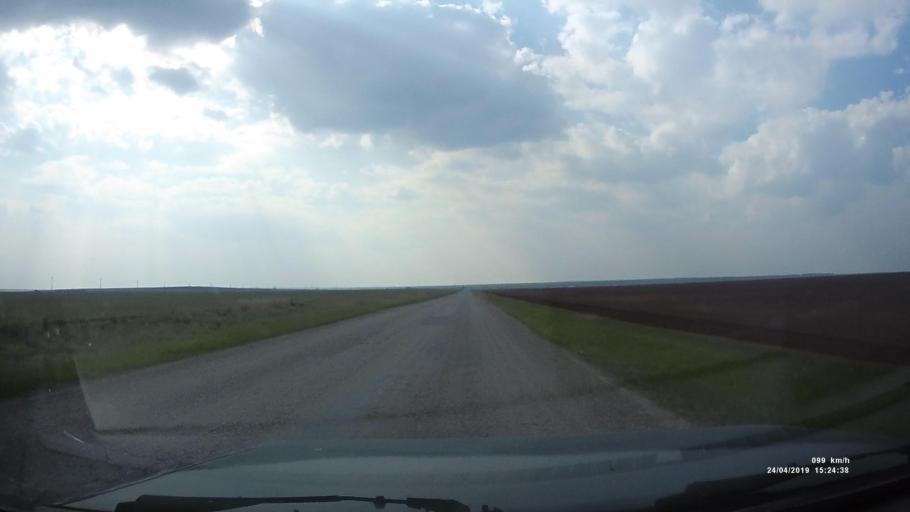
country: RU
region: Rostov
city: Remontnoye
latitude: 46.5488
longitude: 43.0644
